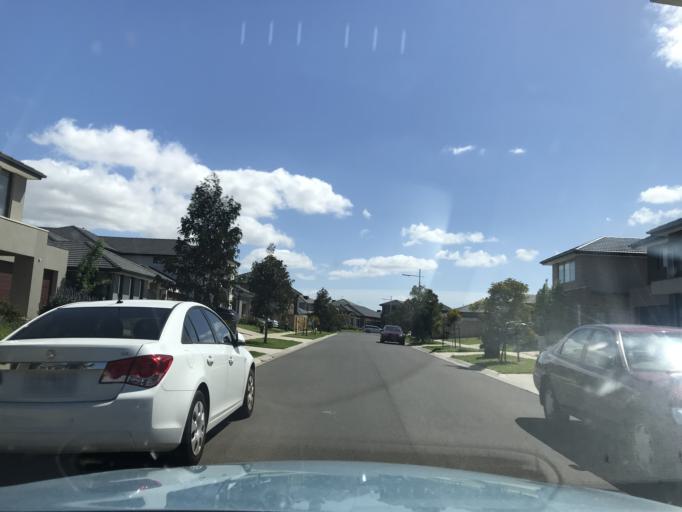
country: AU
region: Victoria
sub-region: Wyndham
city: Williams Landing
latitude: -37.8649
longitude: 144.7376
